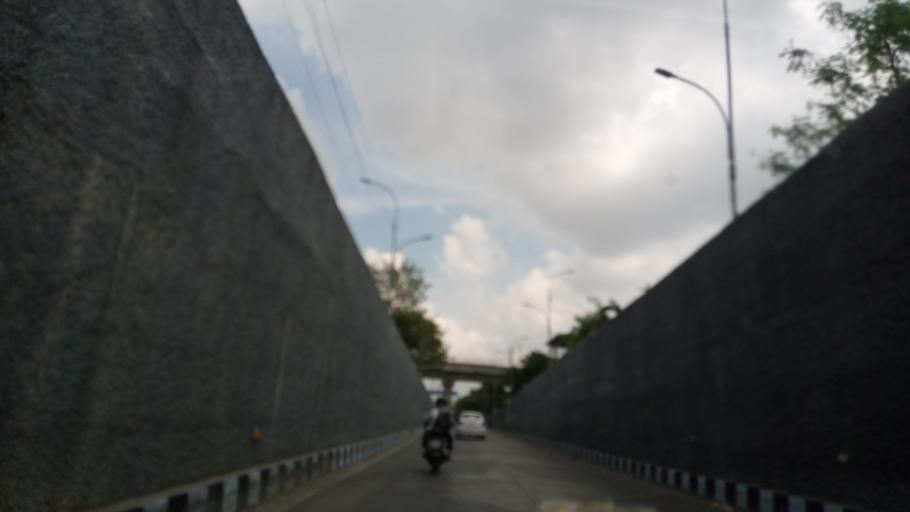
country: IN
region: Tamil Nadu
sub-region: Kancheepuram
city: Saint Thomas Mount
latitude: 12.9859
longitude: 80.1766
